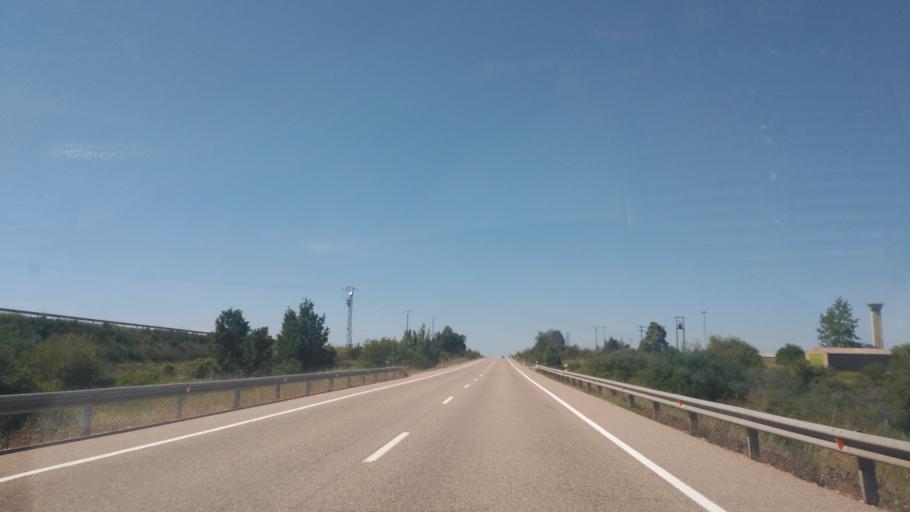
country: ES
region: Castille and Leon
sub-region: Provincia de Salamanca
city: Topas
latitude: 41.1910
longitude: -5.6967
